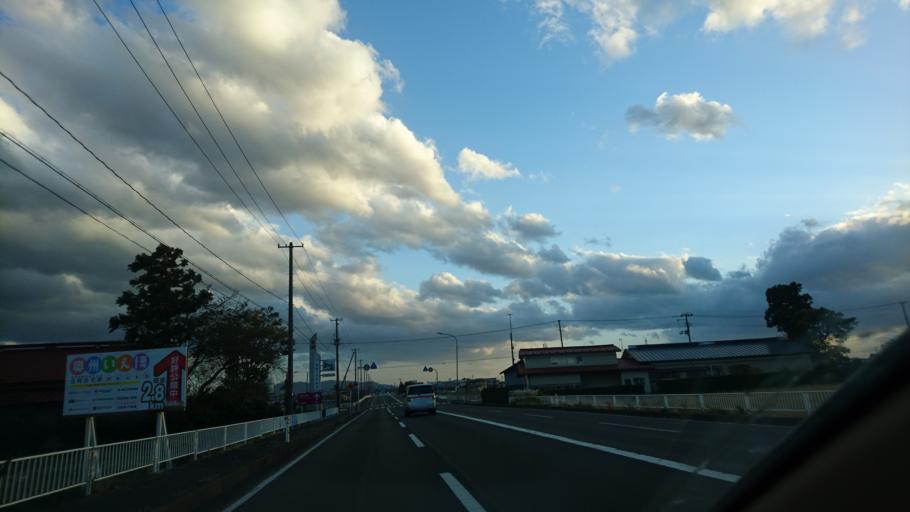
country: JP
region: Iwate
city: Mizusawa
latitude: 39.1608
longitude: 141.1331
